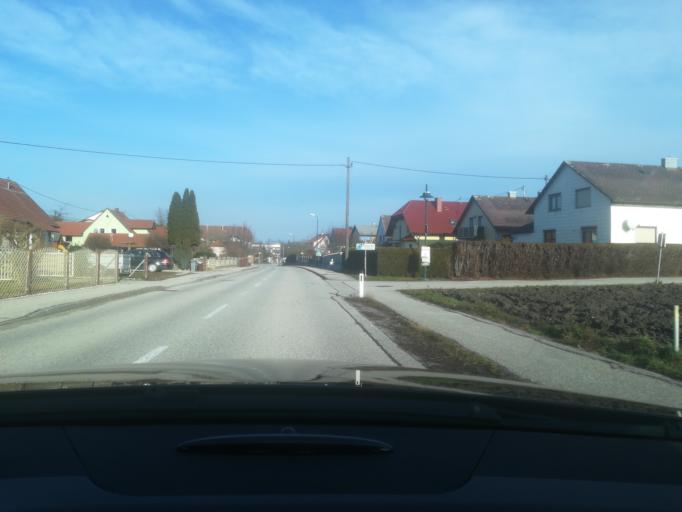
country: AT
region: Upper Austria
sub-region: Wels-Land
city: Buchkirchen
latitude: 48.2797
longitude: 14.0273
